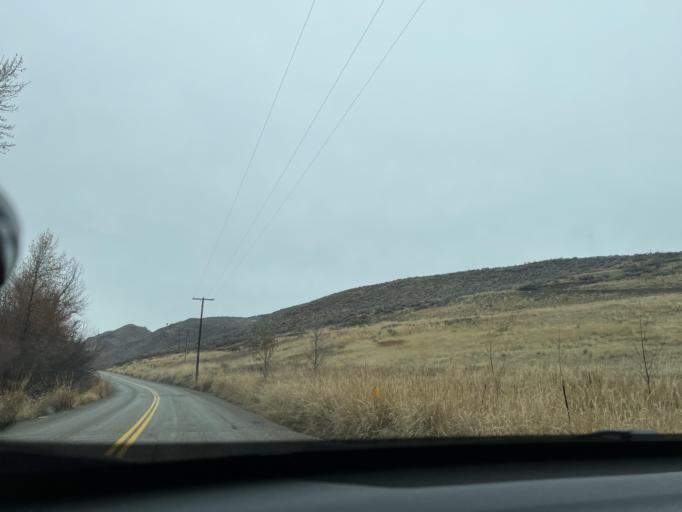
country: US
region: Washington
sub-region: Okanogan County
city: Brewster
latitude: 48.5037
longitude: -120.1739
